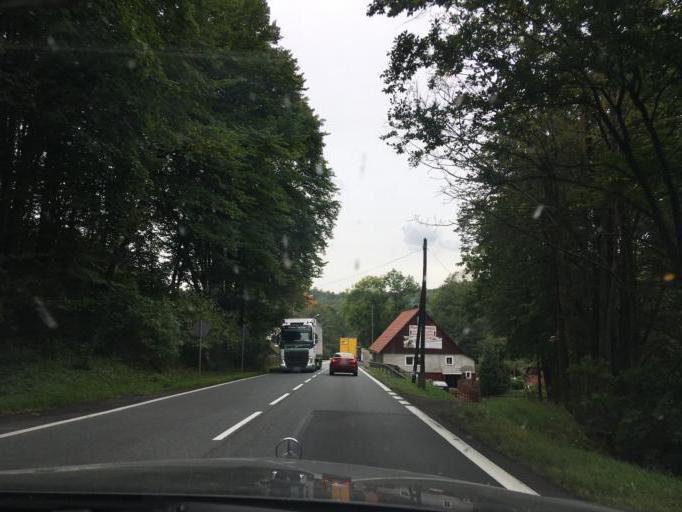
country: PL
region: Lower Silesian Voivodeship
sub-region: Powiat klodzki
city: Lewin Klodzki
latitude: 50.4079
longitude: 16.3000
